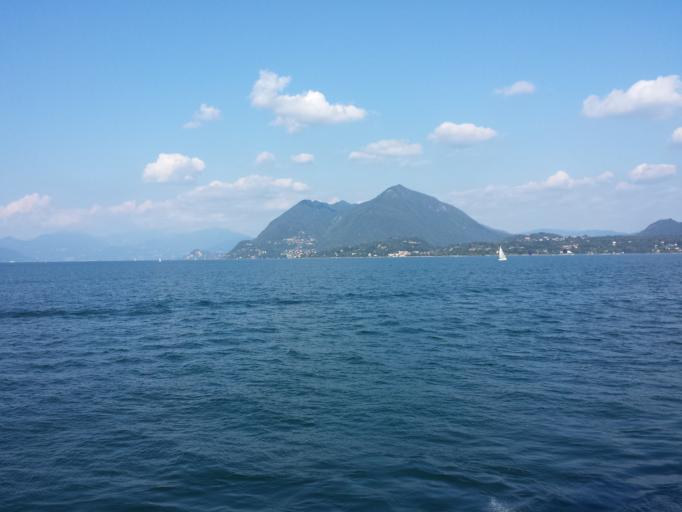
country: IT
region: Piedmont
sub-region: Provincia Verbano-Cusio-Ossola
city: Stresa
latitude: 45.8856
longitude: 8.5507
